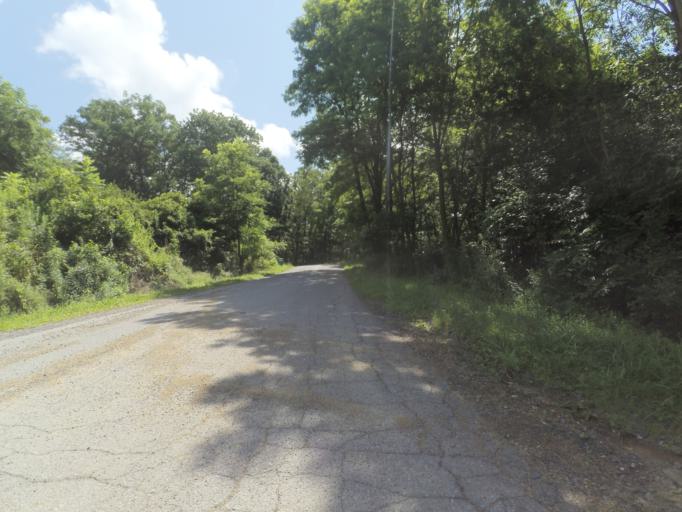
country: US
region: Pennsylvania
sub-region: Centre County
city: Stormstown
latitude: 40.7820
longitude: -78.0461
